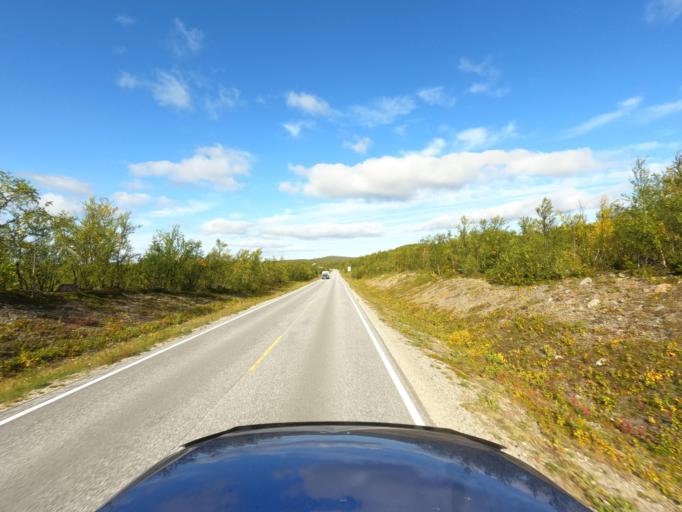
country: NO
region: Finnmark Fylke
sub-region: Karasjok
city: Karasjohka
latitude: 69.5365
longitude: 25.4327
